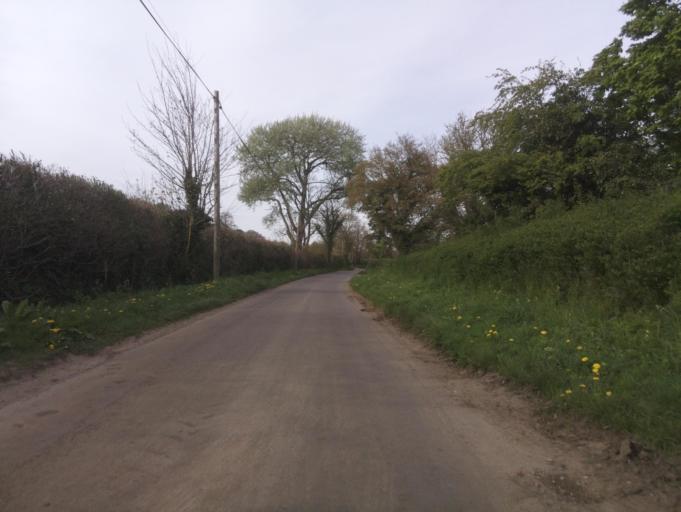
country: GB
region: England
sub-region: Somerset
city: Milborne Port
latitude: 50.9629
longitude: -2.4677
